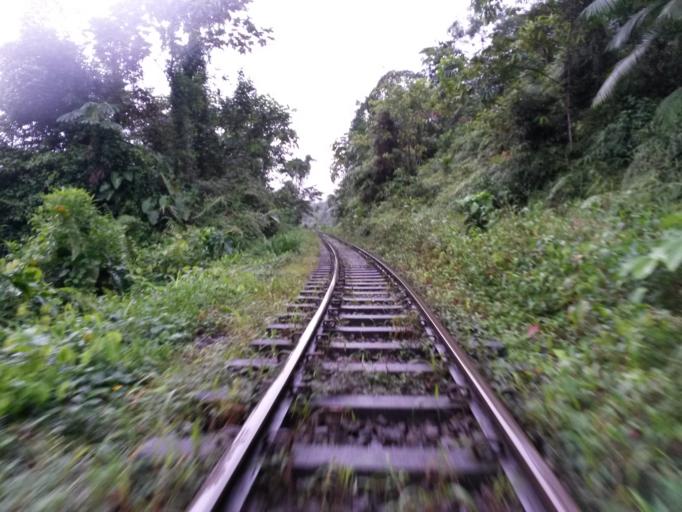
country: CO
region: Valle del Cauca
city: Buenaventura
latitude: 3.8475
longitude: -76.9103
